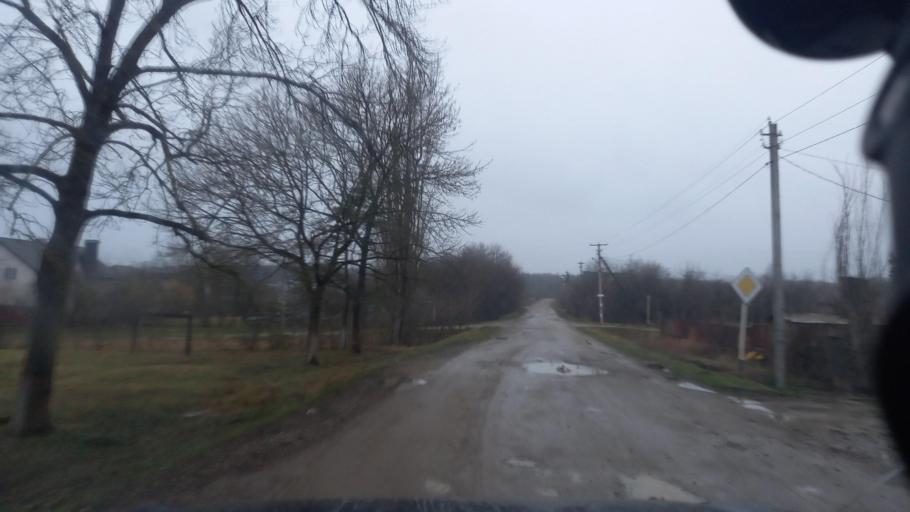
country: RU
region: Krasnodarskiy
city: Saratovskaya
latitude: 44.6474
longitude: 39.3107
